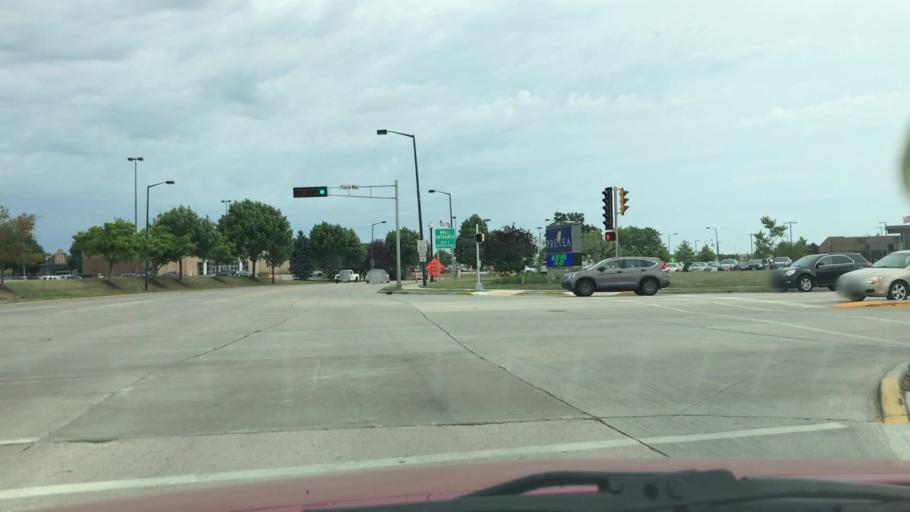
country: US
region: Wisconsin
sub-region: Brown County
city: Ashwaubenon
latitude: 44.4811
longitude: -88.0656
